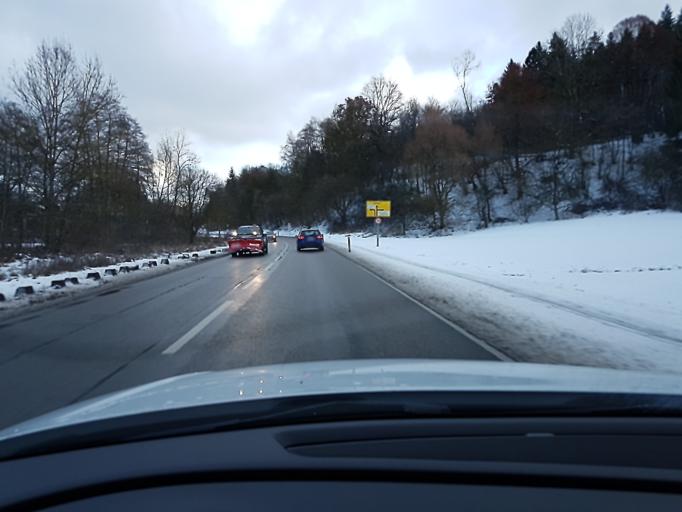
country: DE
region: Baden-Wuerttemberg
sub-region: Regierungsbezirk Stuttgart
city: Murrhardt
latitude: 48.9752
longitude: 9.6000
